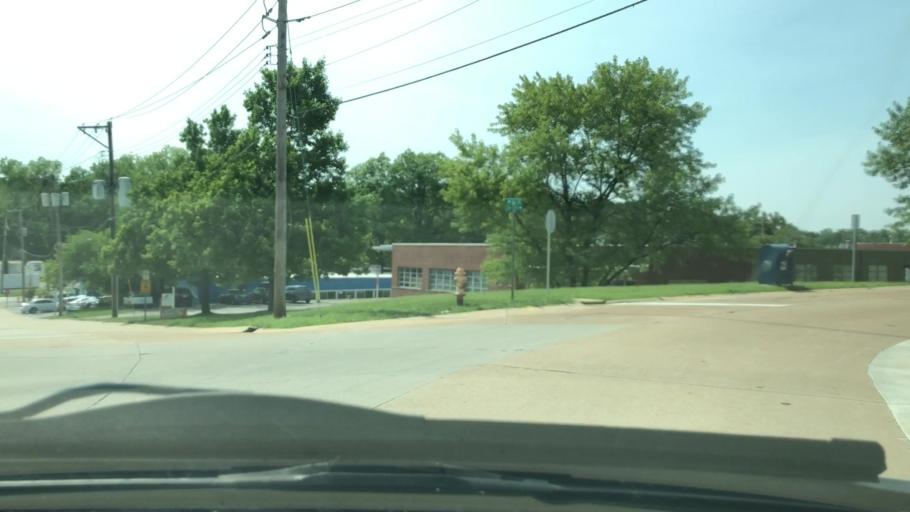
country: US
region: Missouri
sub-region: Saint Louis County
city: Maplewood
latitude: 38.6189
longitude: -90.3355
